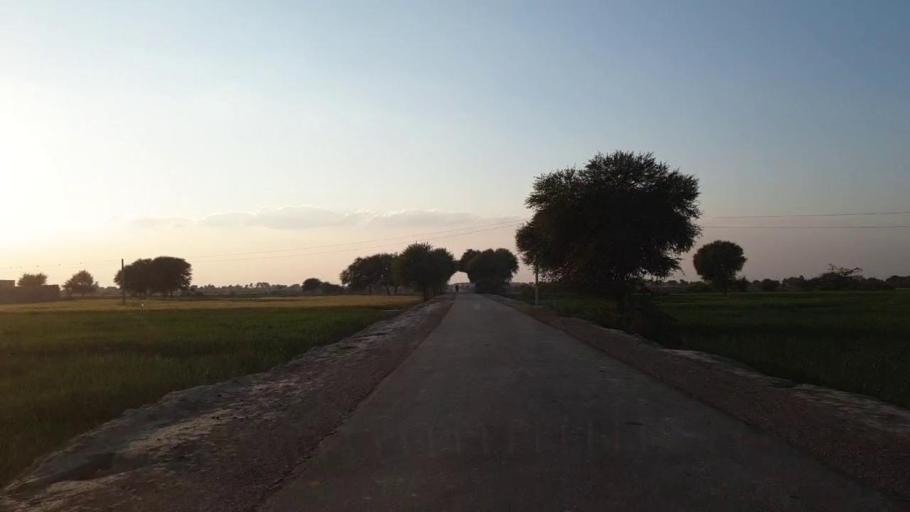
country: PK
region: Sindh
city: Shahpur Chakar
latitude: 26.1563
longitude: 68.5546
